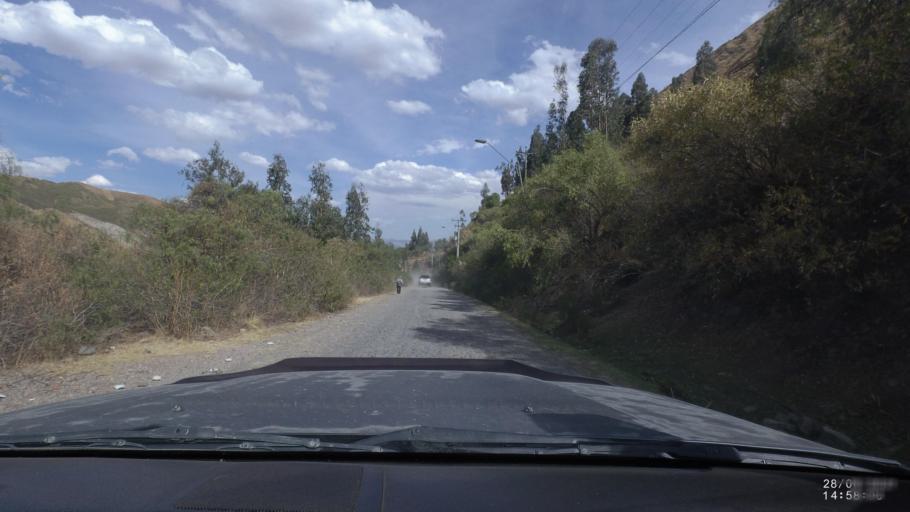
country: BO
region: Cochabamba
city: Cochabamba
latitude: -17.2942
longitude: -66.2986
